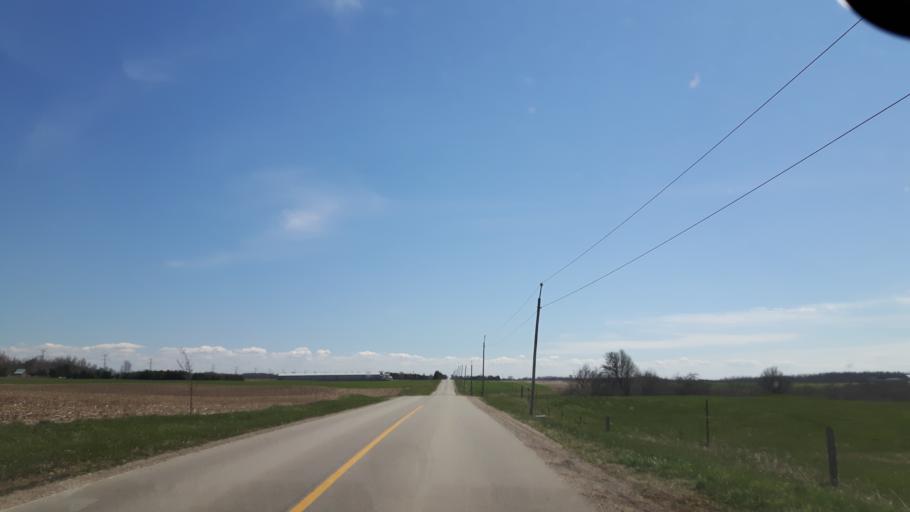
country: CA
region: Ontario
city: Goderich
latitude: 43.6501
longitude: -81.6441
